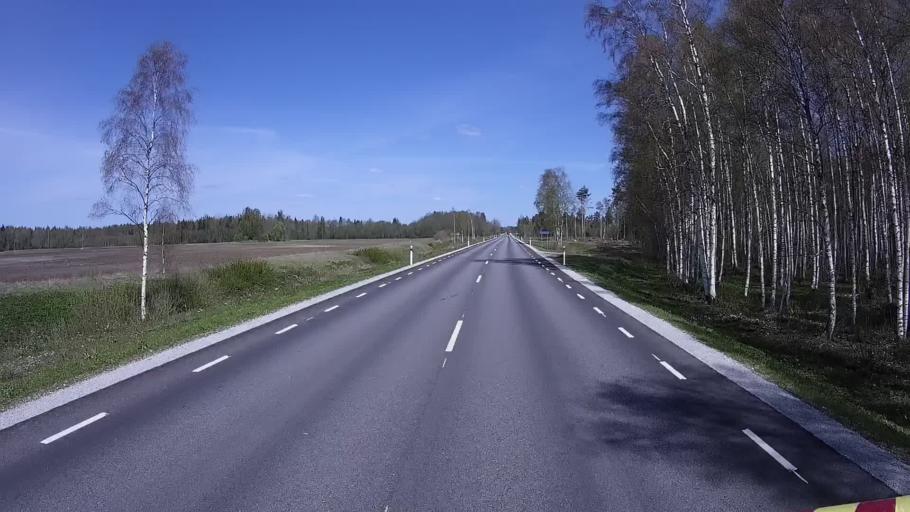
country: EE
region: Harju
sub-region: Nissi vald
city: Turba
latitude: 59.1733
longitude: 24.0764
